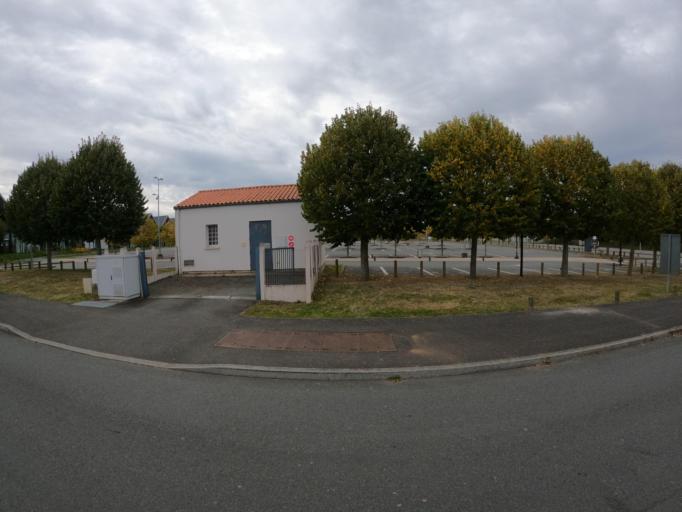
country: FR
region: Pays de la Loire
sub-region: Departement de Maine-et-Loire
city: La Seguiniere
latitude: 47.0556
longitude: -0.9397
